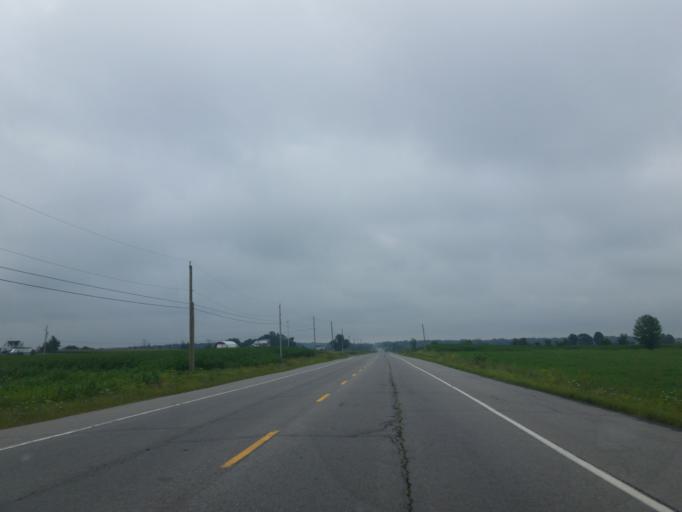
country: CA
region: Ontario
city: Clarence-Rockland
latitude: 45.4094
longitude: -75.4013
